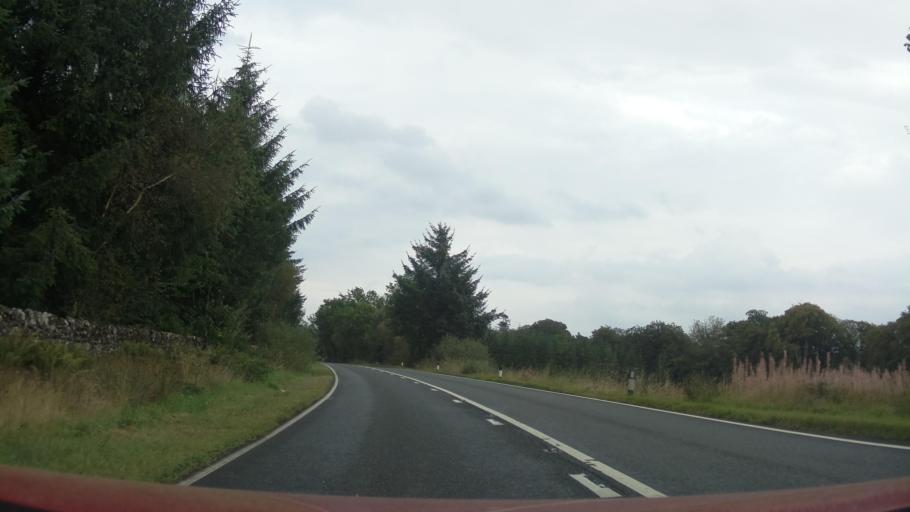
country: GB
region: Scotland
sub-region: Dumfries and Galloway
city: Lochmaben
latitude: 55.2175
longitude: -3.4689
